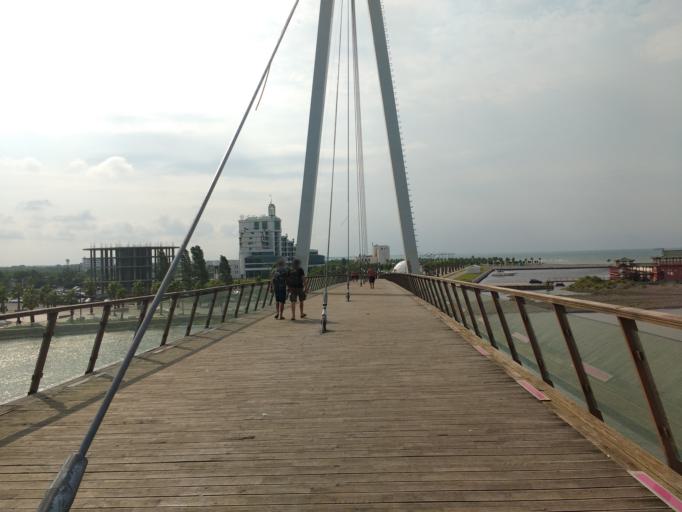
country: GE
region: Samegrelo and Zemo Svaneti
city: P'ot'i
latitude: 42.3926
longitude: 41.5598
